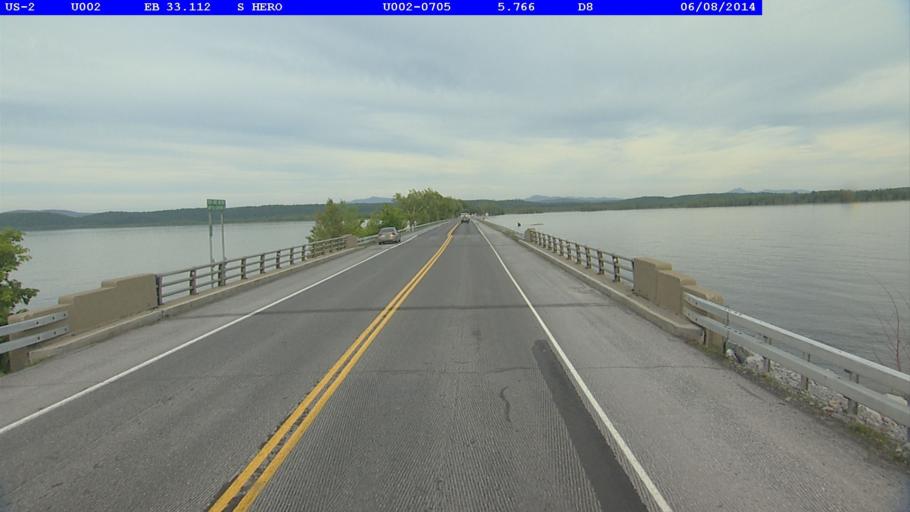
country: US
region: Vermont
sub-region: Chittenden County
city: Colchester
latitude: 44.6316
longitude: -73.2563
